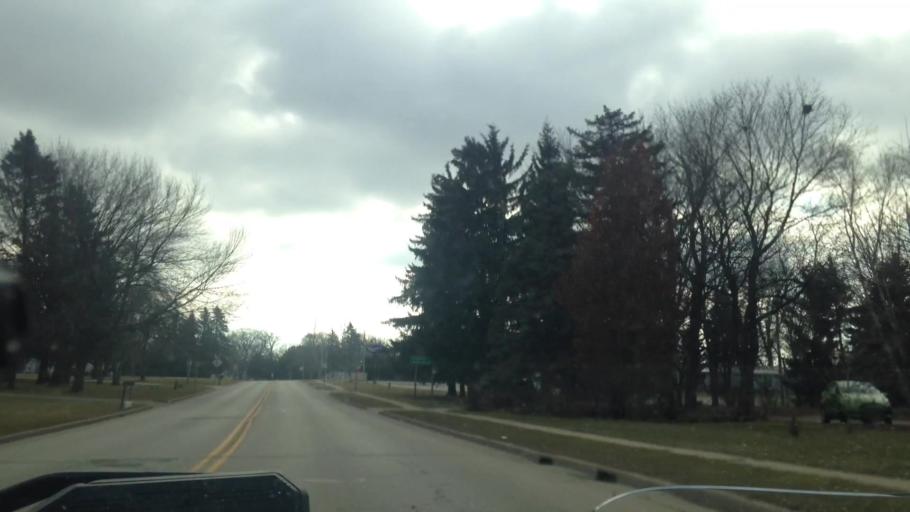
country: US
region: Wisconsin
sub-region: Dodge County
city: Horicon
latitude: 43.4488
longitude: -88.6208
